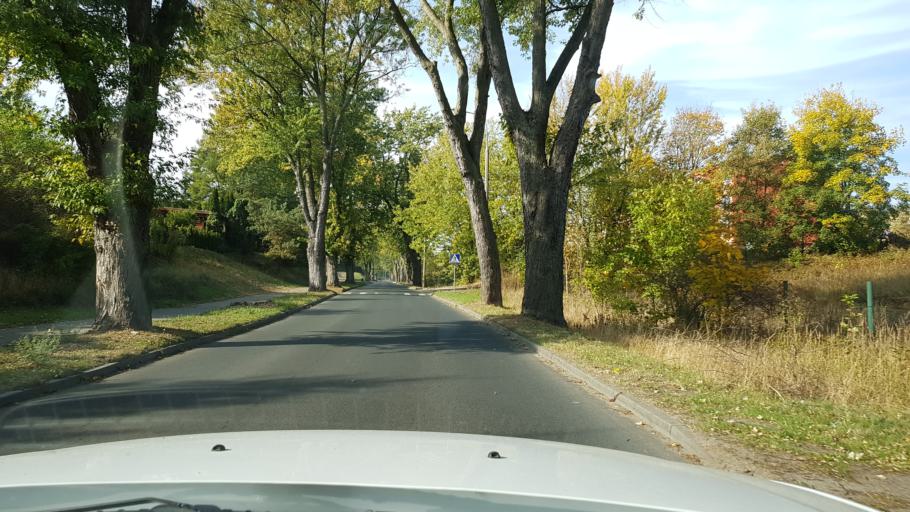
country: PL
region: West Pomeranian Voivodeship
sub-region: Powiat mysliborski
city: Barlinek
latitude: 52.9854
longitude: 15.1947
